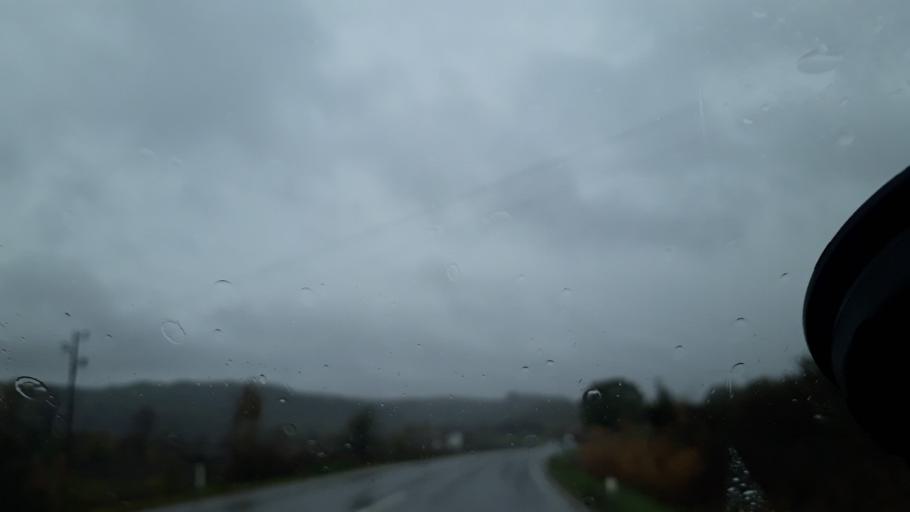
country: BA
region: Republika Srpska
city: Maglajani
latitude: 44.8614
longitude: 17.4620
